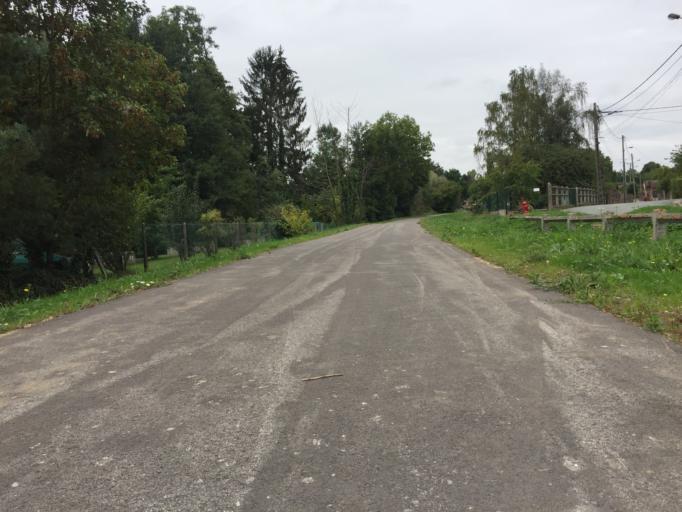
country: FR
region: Picardie
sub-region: Departement de l'Oise
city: Saint-Paul
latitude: 49.4038
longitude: 2.0088
